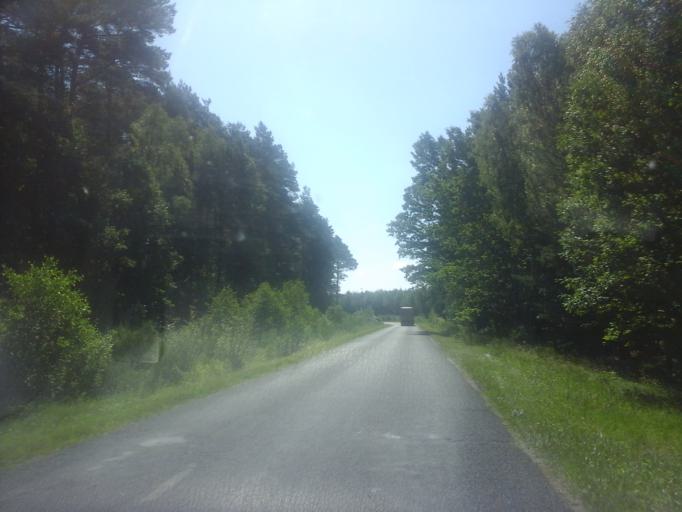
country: PL
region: West Pomeranian Voivodeship
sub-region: Powiat bialogardzki
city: Bialogard
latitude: 54.0337
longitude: 16.1374
